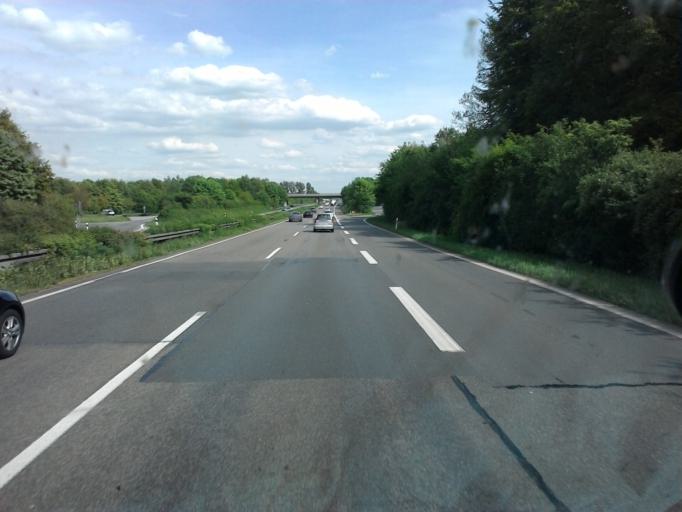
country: DE
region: North Rhine-Westphalia
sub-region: Regierungsbezirk Dusseldorf
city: Alpen
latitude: 51.5585
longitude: 6.5257
